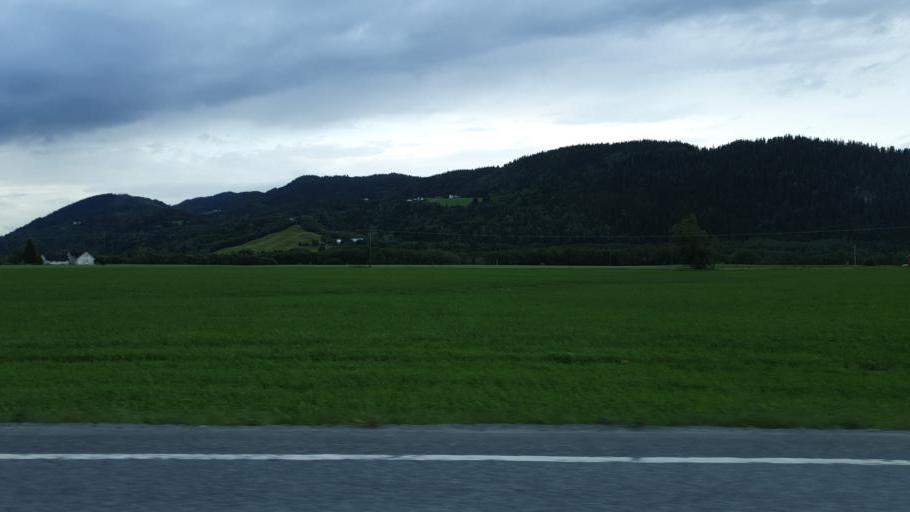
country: NO
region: Sor-Trondelag
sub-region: Melhus
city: Lundamo
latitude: 63.1823
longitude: 10.3156
